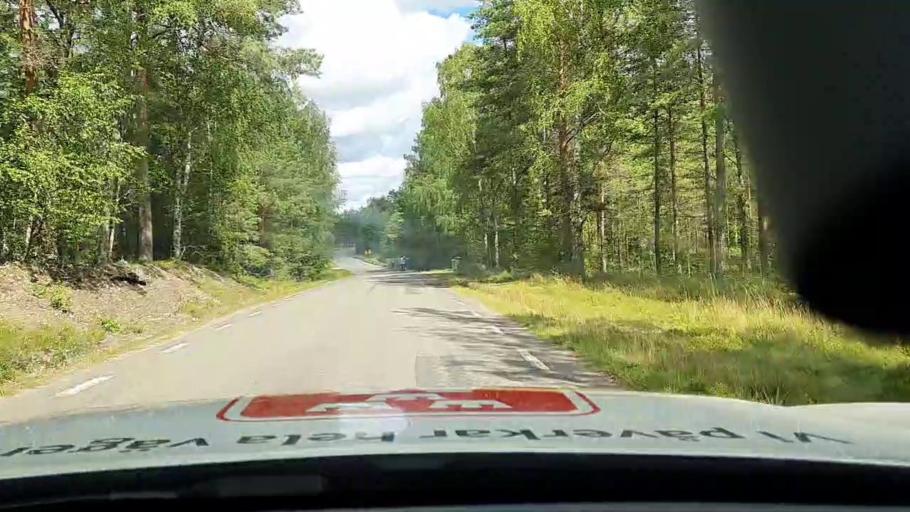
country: SE
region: Vaestra Goetaland
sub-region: Karlsborgs Kommun
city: Molltorp
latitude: 58.6036
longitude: 14.3787
